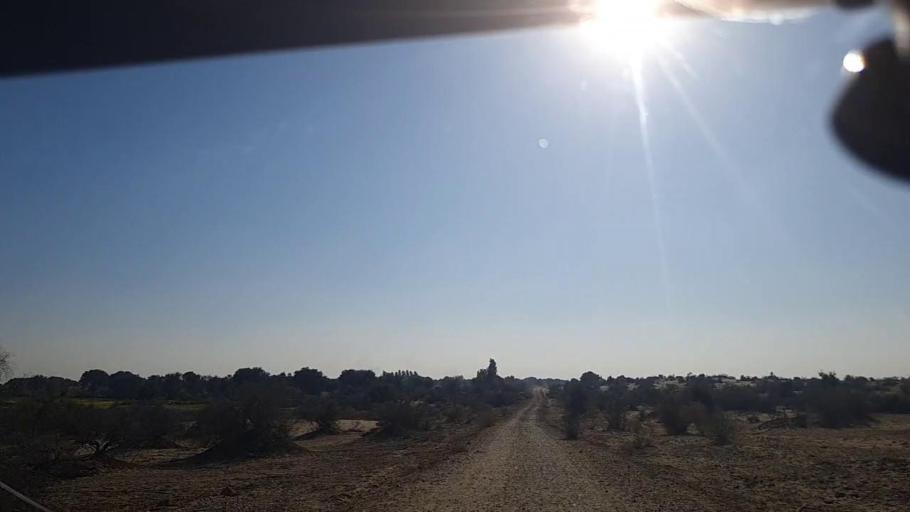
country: PK
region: Sindh
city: Khanpur
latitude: 27.6398
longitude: 69.4049
